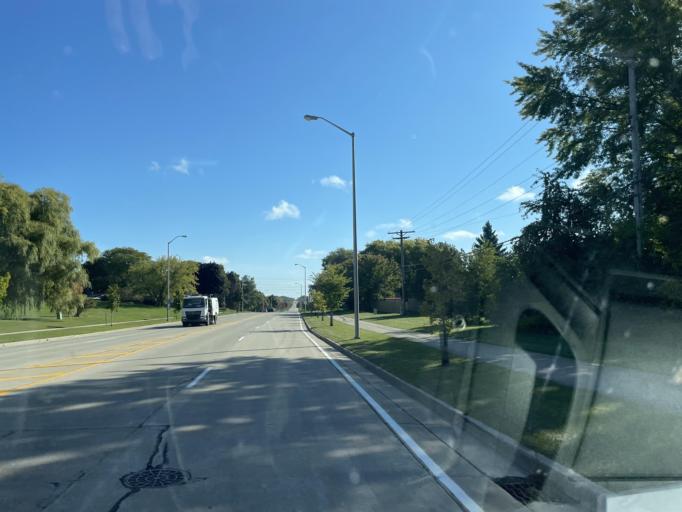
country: US
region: Wisconsin
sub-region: Milwaukee County
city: Oak Creek
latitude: 42.9010
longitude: -87.9094
